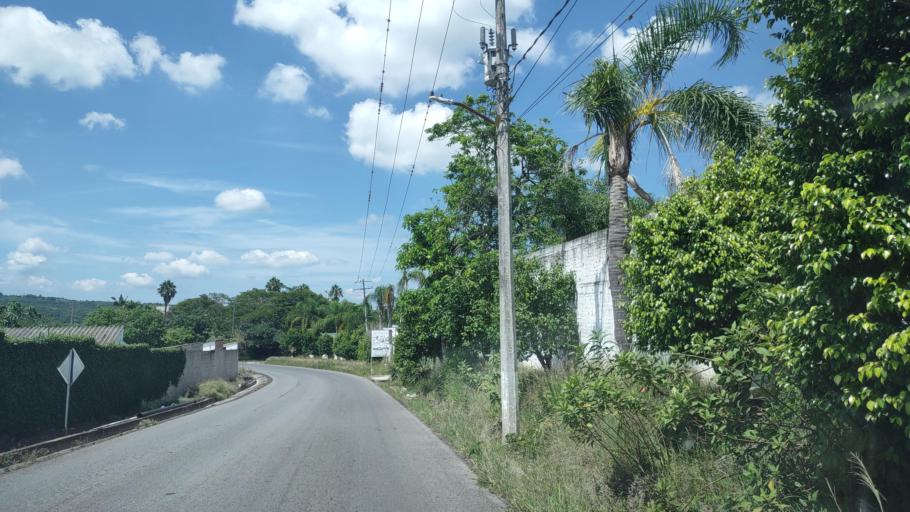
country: MX
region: Veracruz
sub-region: Emiliano Zapata
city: Dos Rios
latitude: 19.4948
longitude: -96.8045
